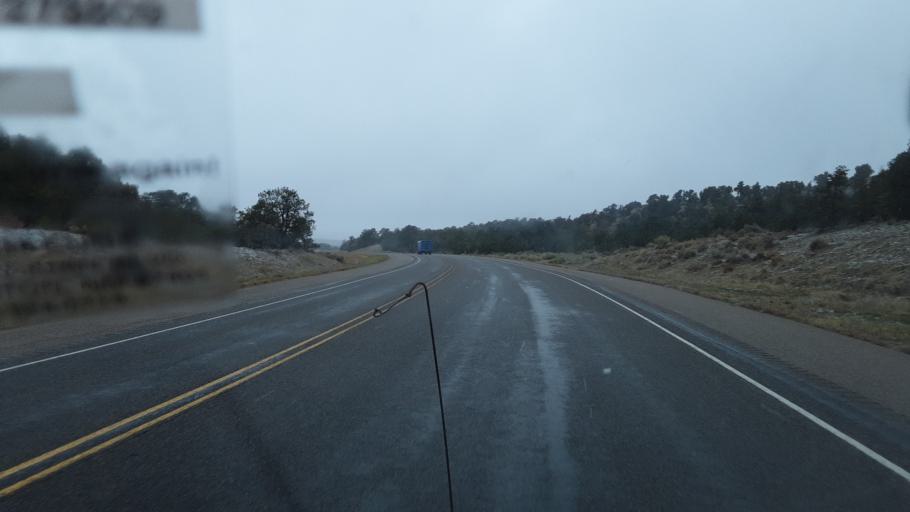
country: US
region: New Mexico
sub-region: Rio Arriba County
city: Tierra Amarilla
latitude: 36.4680
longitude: -106.4811
